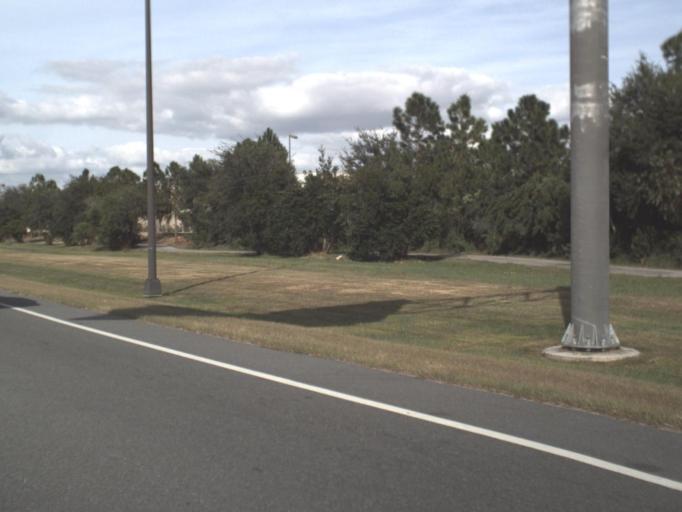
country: US
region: Florida
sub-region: Orange County
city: Hunters Creek
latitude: 28.3383
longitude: -81.4196
